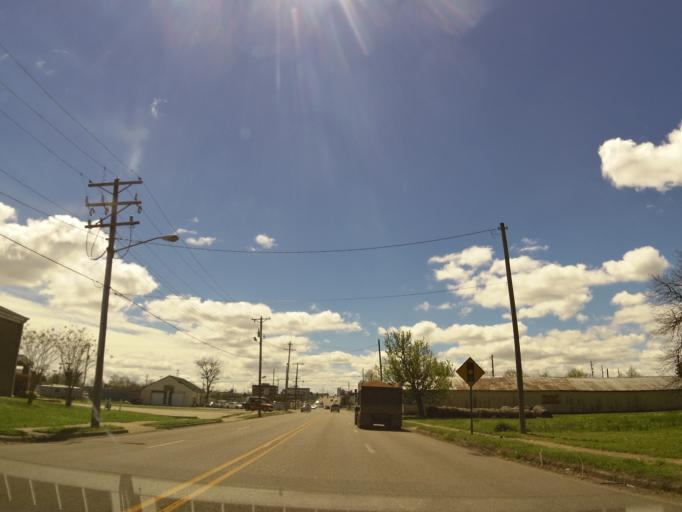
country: US
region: Arkansas
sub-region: Craighead County
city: Jonesboro
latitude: 35.8477
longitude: -90.7047
